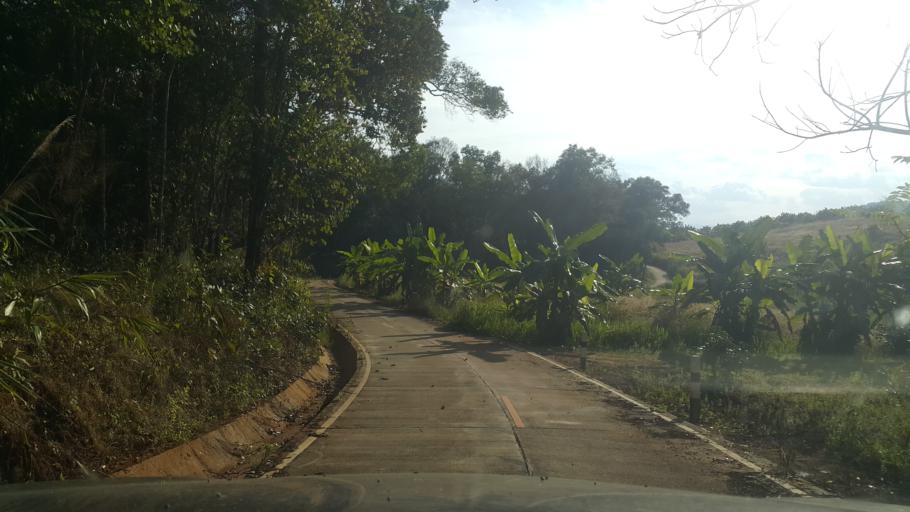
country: TH
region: Chiang Mai
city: Samoeng
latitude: 19.0033
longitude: 98.6864
